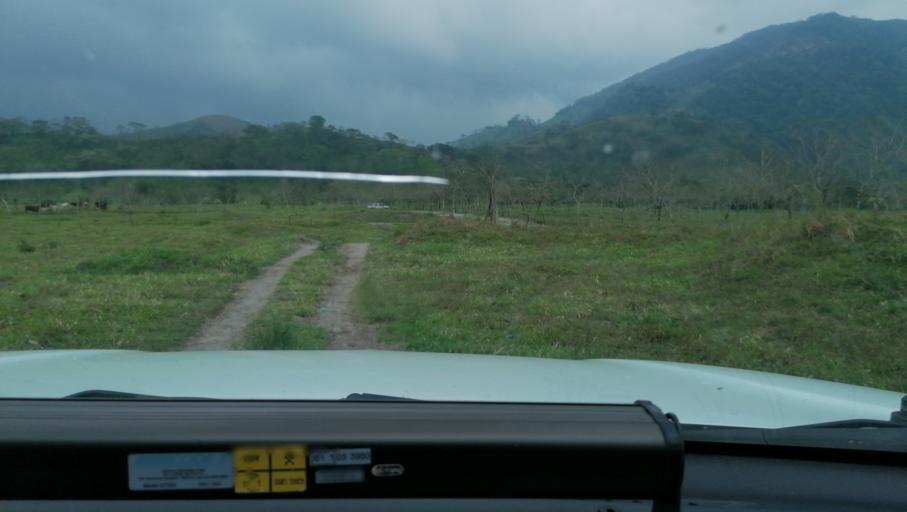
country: MX
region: Chiapas
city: Ixtacomitan
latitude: 17.3646
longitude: -93.1851
